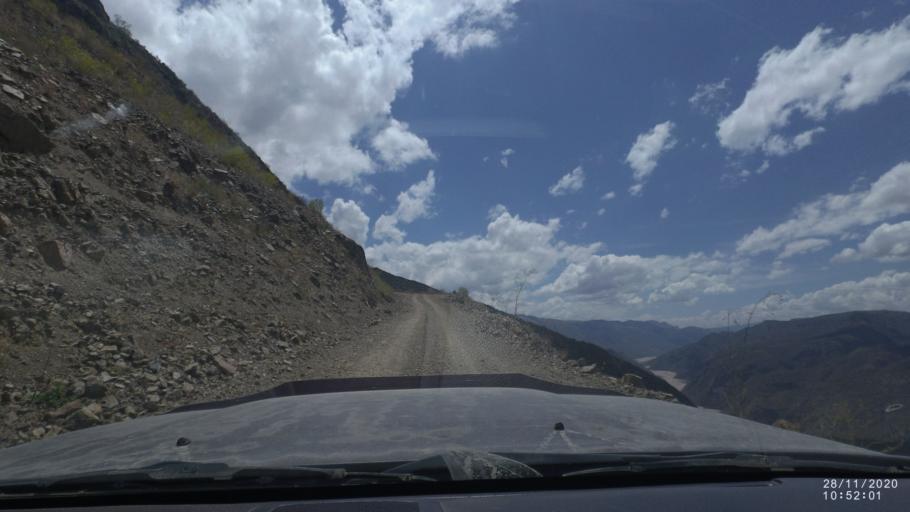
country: BO
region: Cochabamba
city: Capinota
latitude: -17.7853
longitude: -66.1217
